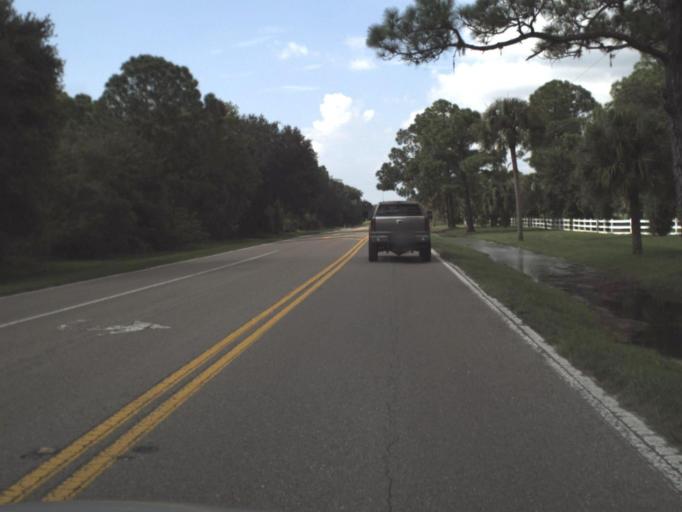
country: US
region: Florida
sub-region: Sarasota County
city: Plantation
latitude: 27.0684
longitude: -82.3221
